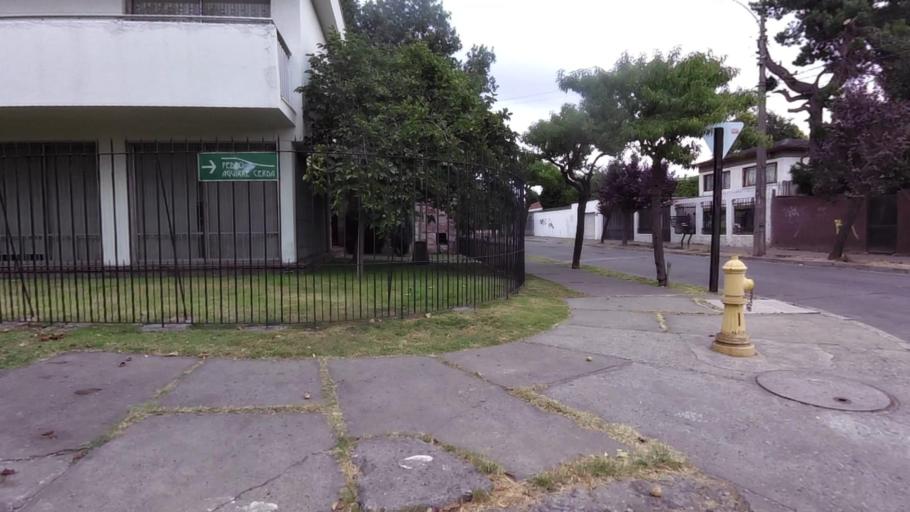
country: CL
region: O'Higgins
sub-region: Provincia de Cachapoal
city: Rancagua
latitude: -34.1627
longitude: -70.7459
